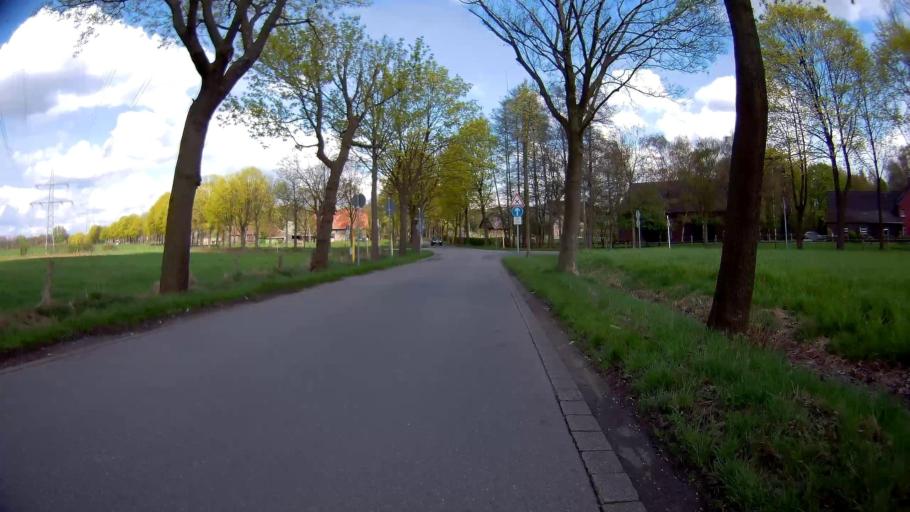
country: DE
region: North Rhine-Westphalia
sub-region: Regierungsbezirk Munster
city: Gladbeck
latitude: 51.5660
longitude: 7.0203
